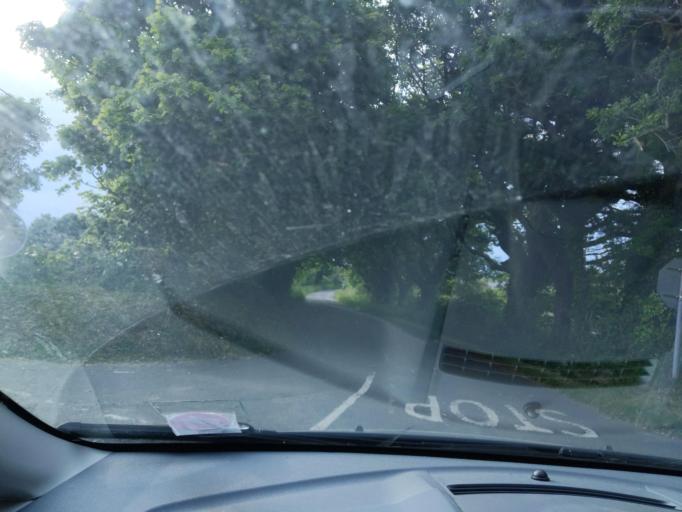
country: IM
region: Ramsey
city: Ramsey
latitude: 54.3482
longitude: -4.4490
